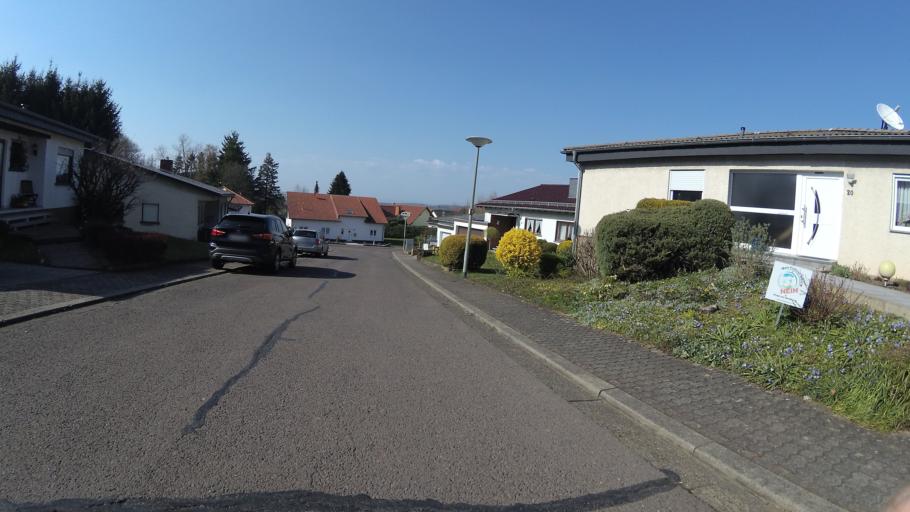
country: DE
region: Saarland
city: Heusweiler
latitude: 49.3269
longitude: 6.9863
